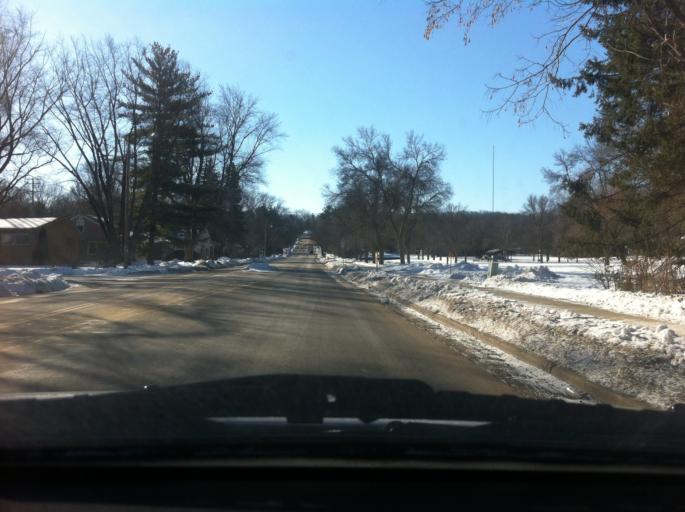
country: US
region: Wisconsin
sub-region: Dane County
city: Shorewood Hills
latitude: 43.0745
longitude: -89.4781
